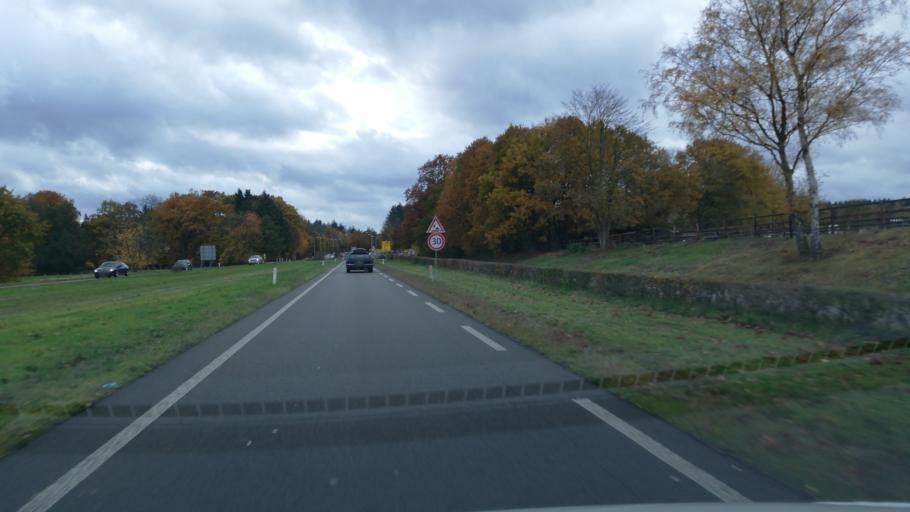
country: NL
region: Gelderland
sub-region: Gemeente Apeldoorn
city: Beekbergen
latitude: 52.1800
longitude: 5.9140
